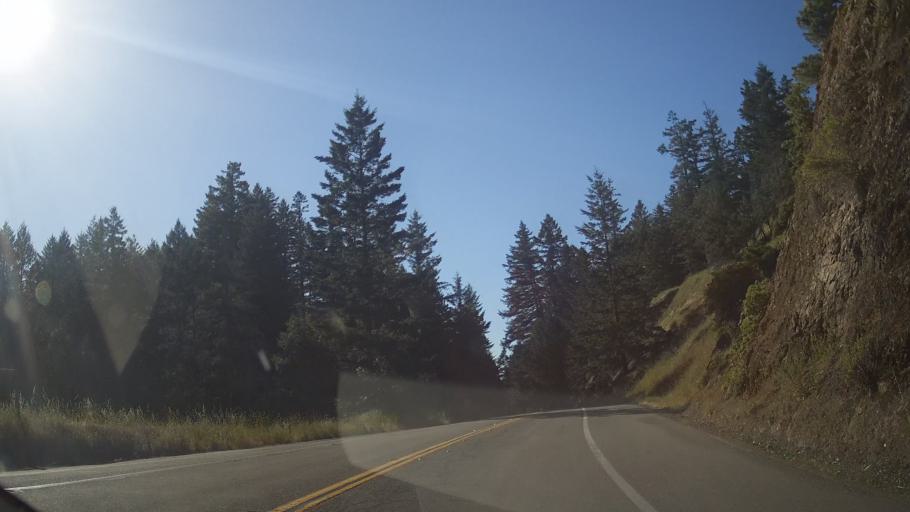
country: US
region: California
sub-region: Mendocino County
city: Brooktrails
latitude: 39.3887
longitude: -123.4425
